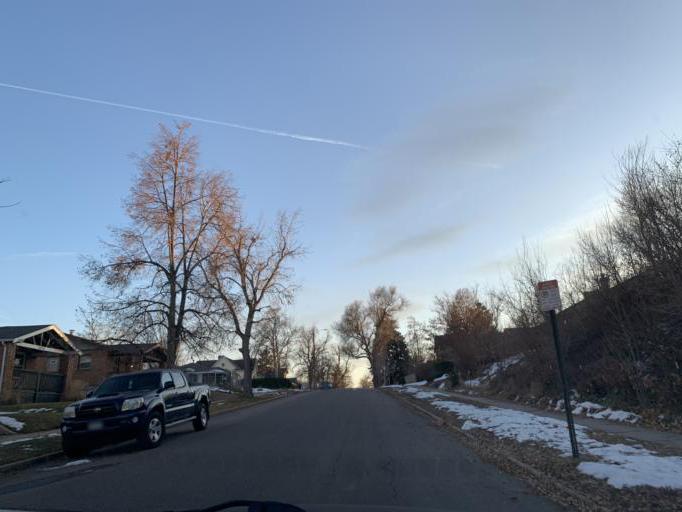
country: US
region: Colorado
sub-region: Adams County
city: Berkley
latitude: 39.7891
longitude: -105.0428
